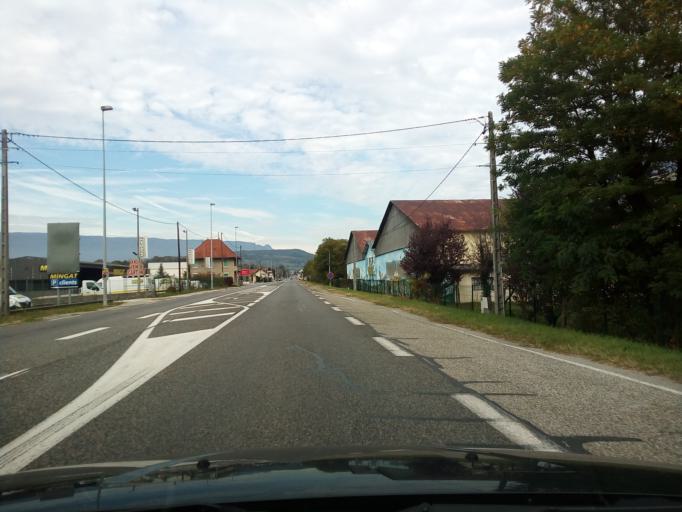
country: FR
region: Rhone-Alpes
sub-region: Departement de la Savoie
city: La Ravoire
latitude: 45.5588
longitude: 5.9741
